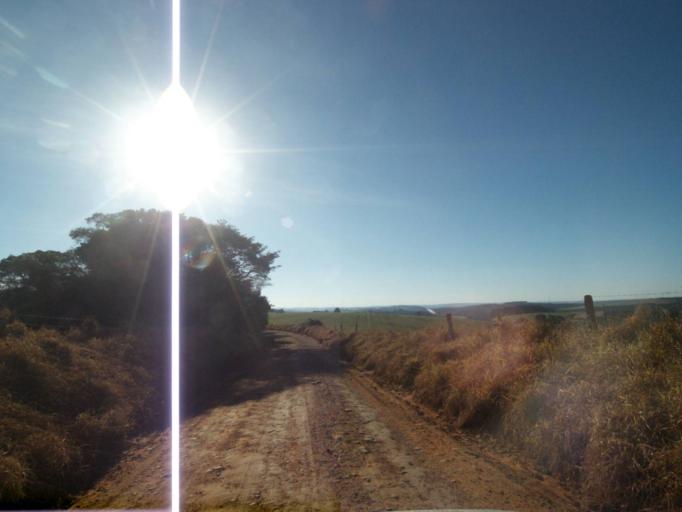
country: BR
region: Parana
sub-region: Telemaco Borba
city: Telemaco Borba
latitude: -24.5338
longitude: -50.6285
